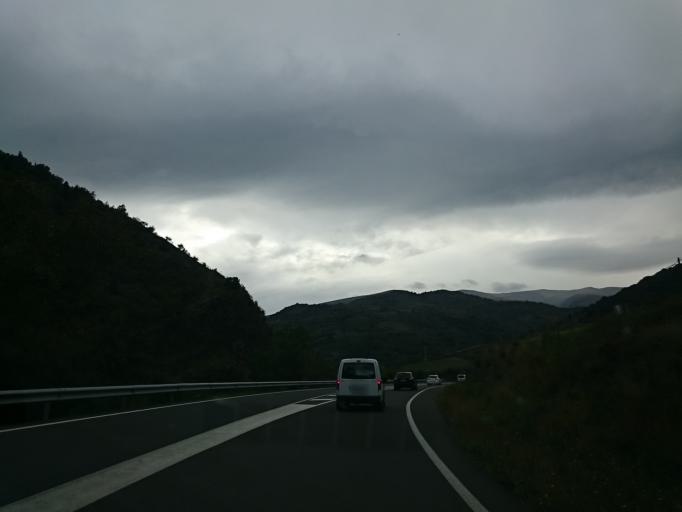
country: ES
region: Catalonia
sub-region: Provincia de Lleida
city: Sort
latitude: 42.4481
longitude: 1.1430
